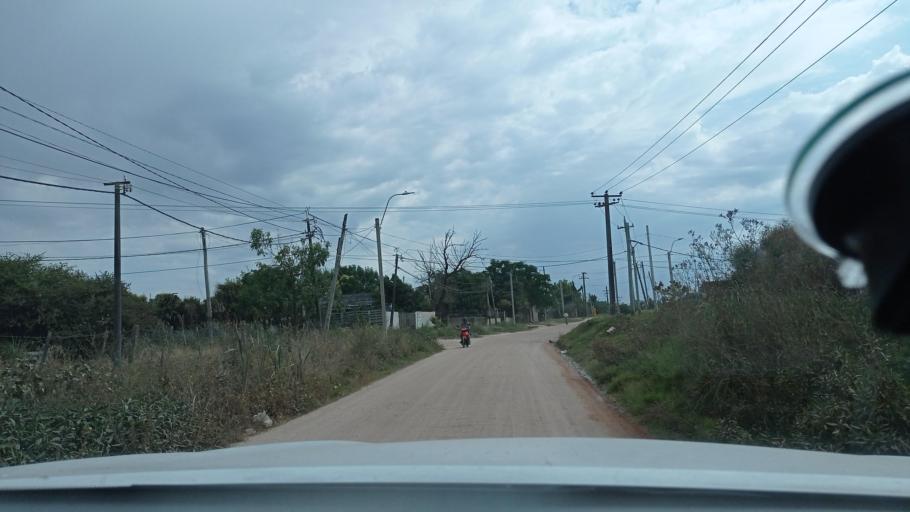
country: UY
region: Canelones
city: Pando
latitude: -34.7209
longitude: -55.9723
